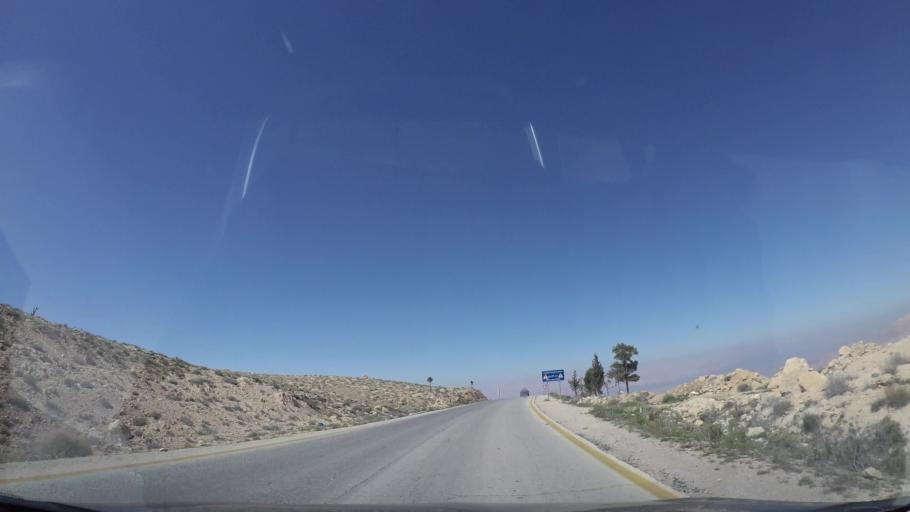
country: JO
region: Tafielah
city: At Tafilah
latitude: 30.8592
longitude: 35.5405
